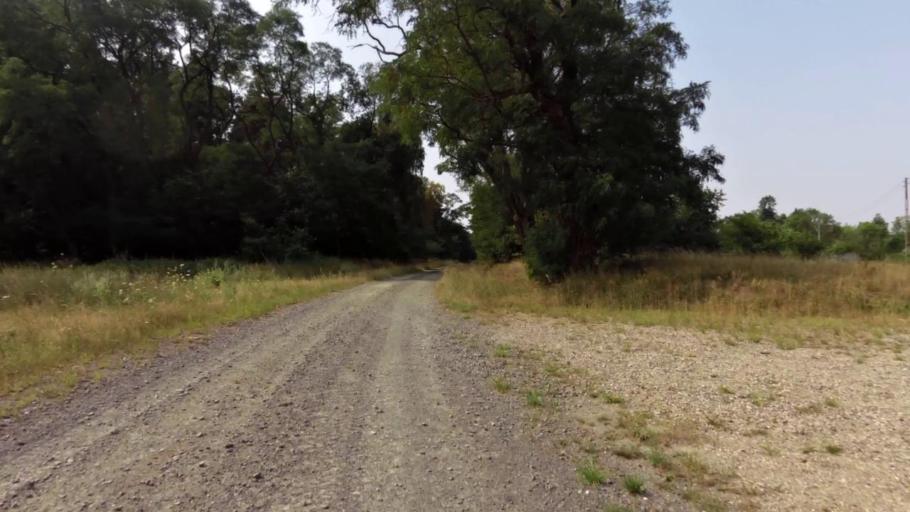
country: PL
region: West Pomeranian Voivodeship
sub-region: Powiat gryfinski
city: Mieszkowice
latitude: 52.8433
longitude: 14.5441
